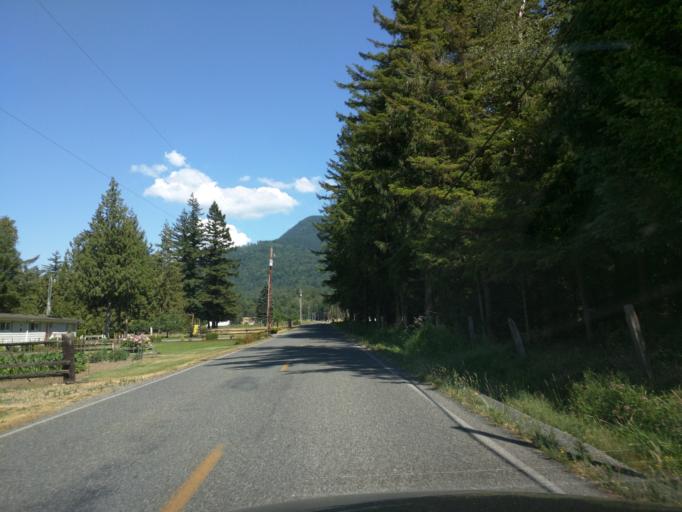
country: US
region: Washington
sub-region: Whatcom County
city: Nooksack
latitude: 48.9203
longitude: -122.2842
